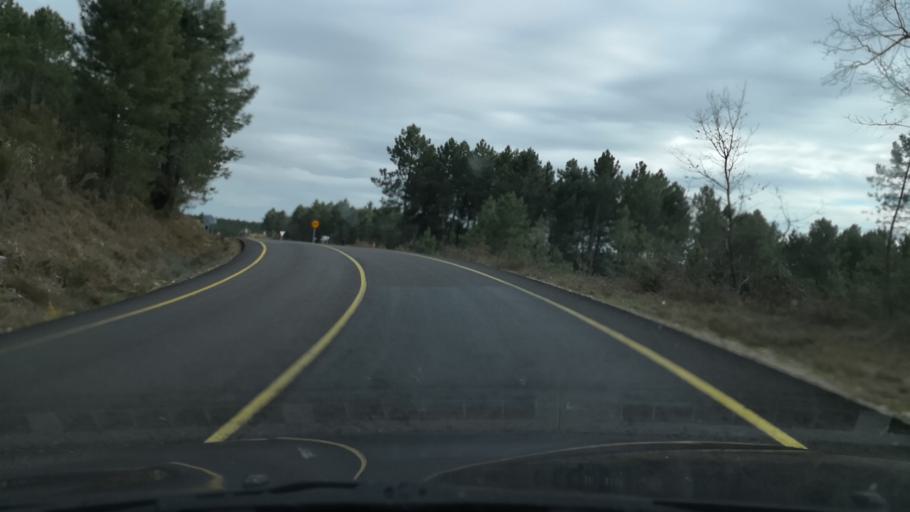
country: ES
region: Castille and Leon
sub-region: Provincia de Salamanca
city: Penaparda
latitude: 40.2657
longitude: -6.6904
